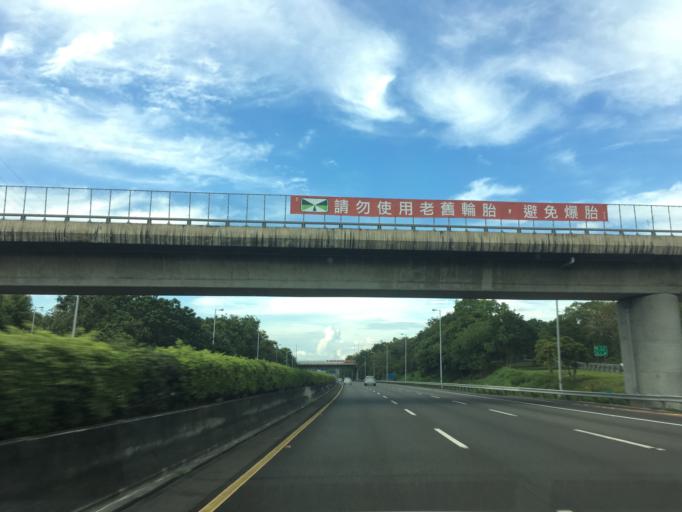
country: TW
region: Taiwan
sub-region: Yunlin
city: Douliu
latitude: 23.5923
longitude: 120.5210
